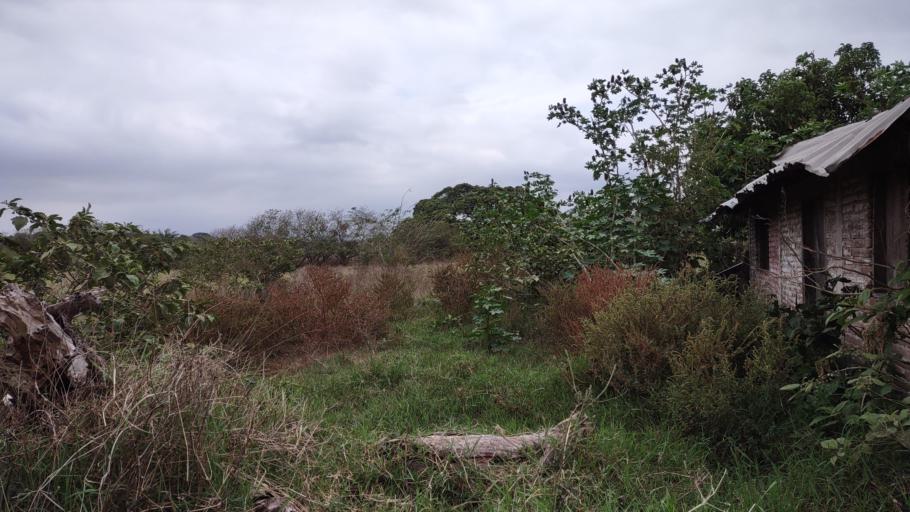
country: MX
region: Veracruz
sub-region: Veracruz
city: Delfino Victoria (Santa Fe)
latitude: 19.2695
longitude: -96.2998
